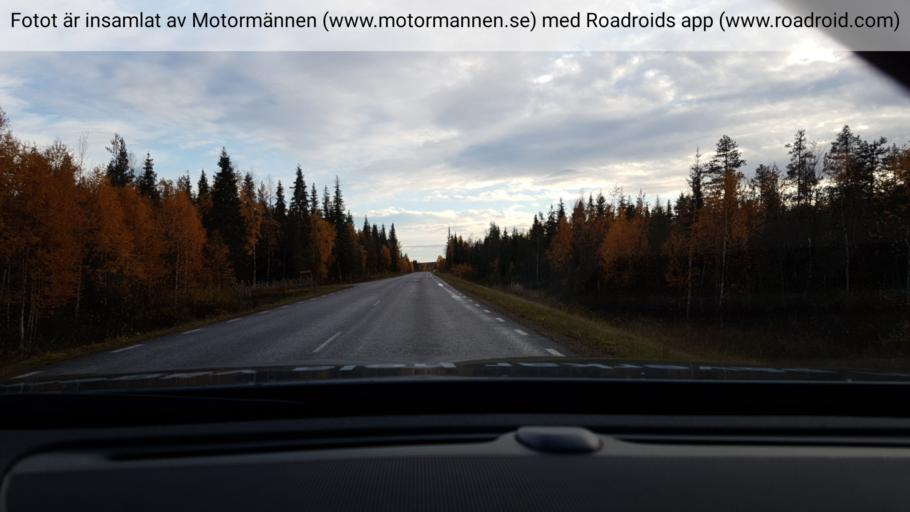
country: SE
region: Norrbotten
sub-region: Overkalix Kommun
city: OEverkalix
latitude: 66.9038
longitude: 22.7755
